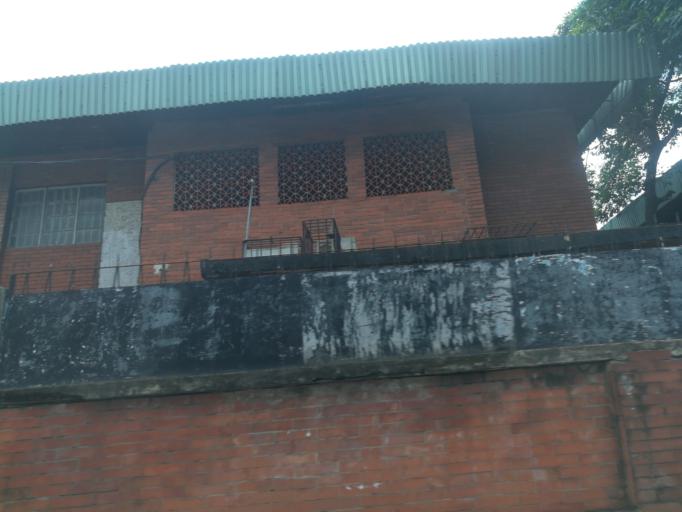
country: NG
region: Lagos
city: Somolu
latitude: 6.5520
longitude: 3.3634
